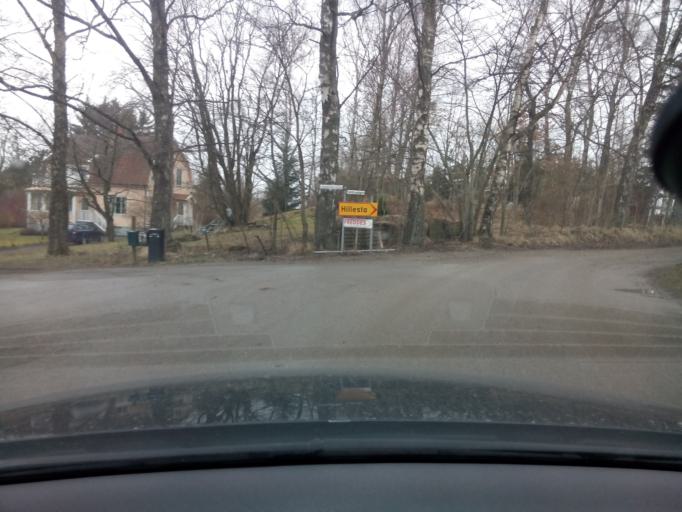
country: SE
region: Soedermanland
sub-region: Trosa Kommun
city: Vagnharad
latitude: 58.9222
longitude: 17.4485
